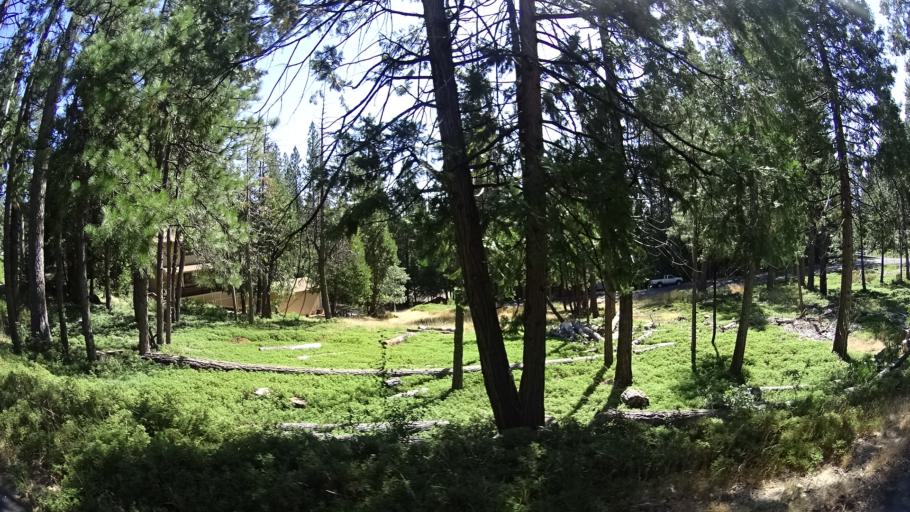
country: US
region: California
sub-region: Calaveras County
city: Arnold
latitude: 38.2494
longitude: -120.3695
